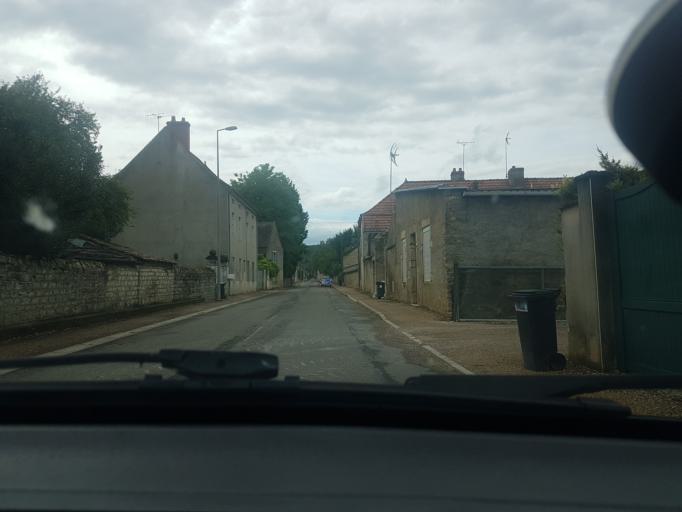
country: FR
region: Bourgogne
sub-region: Departement de Saone-et-Loire
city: Fontaines
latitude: 46.8497
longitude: 4.7680
